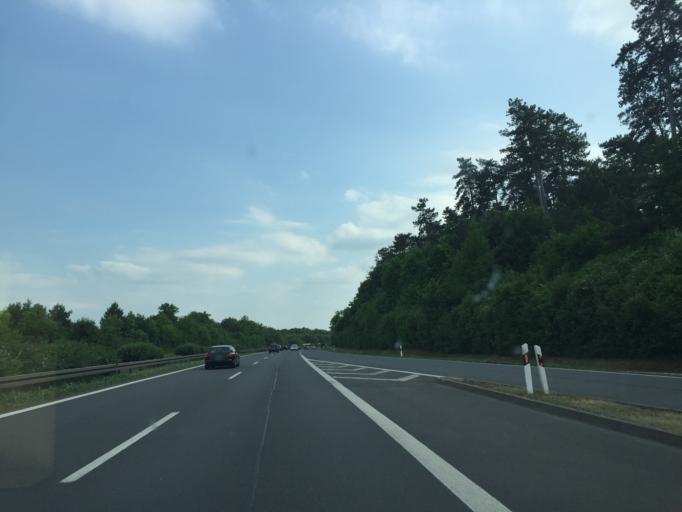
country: DE
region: Baden-Wuerttemberg
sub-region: Regierungsbezirk Stuttgart
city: Grunsfeld
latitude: 49.6272
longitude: 9.7295
